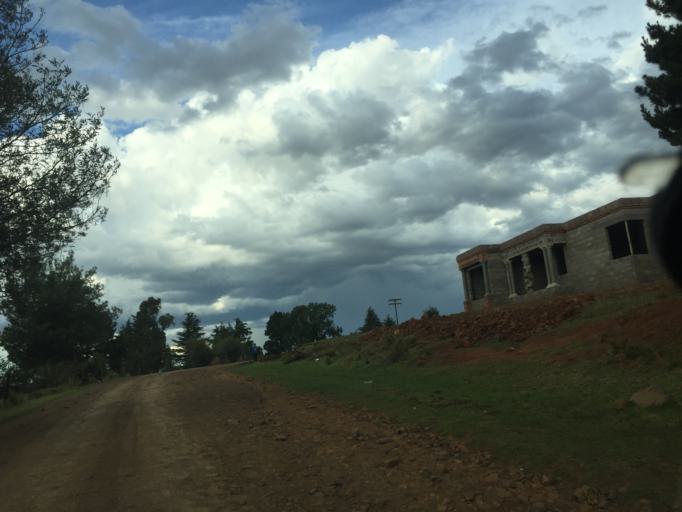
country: LS
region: Leribe
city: Leribe
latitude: -29.1565
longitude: 28.0352
